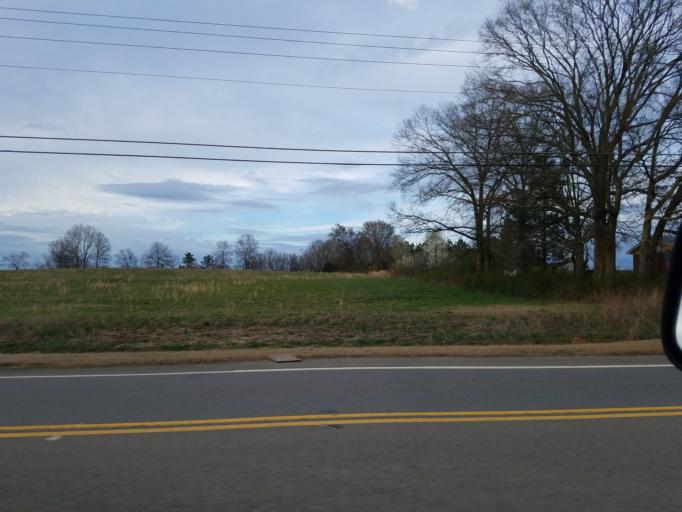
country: US
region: Georgia
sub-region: Bartow County
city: Adairsville
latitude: 34.4482
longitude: -84.8331
